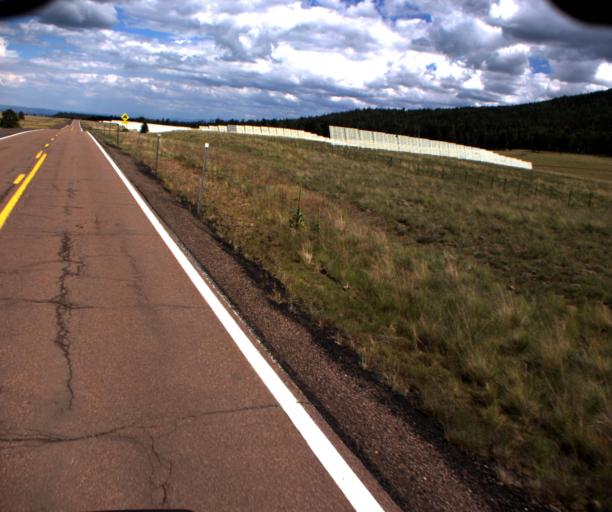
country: US
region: Arizona
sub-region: Apache County
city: Eagar
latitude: 34.0520
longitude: -109.5260
